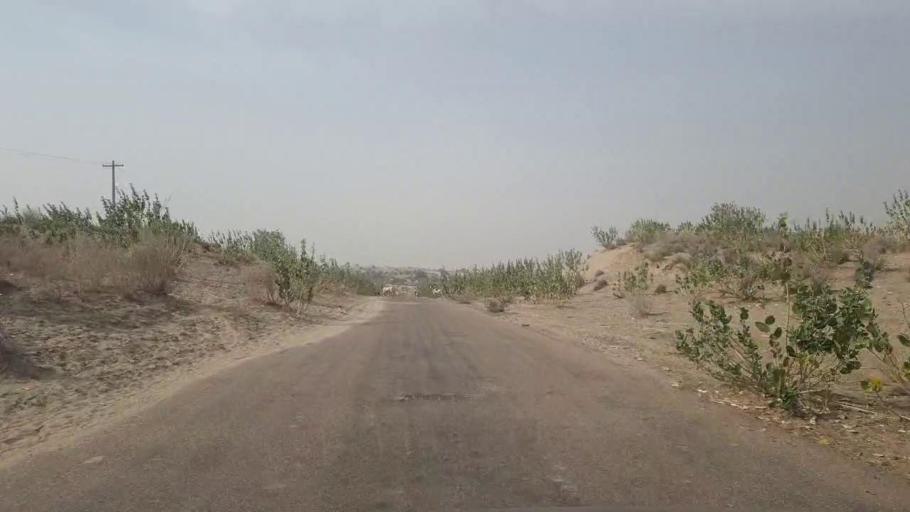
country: PK
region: Sindh
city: Chor
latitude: 25.6165
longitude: 69.9294
